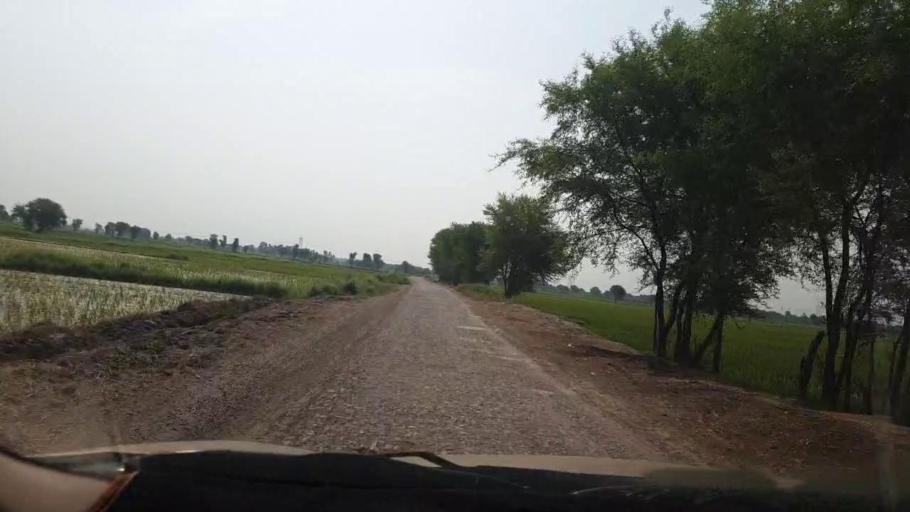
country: PK
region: Sindh
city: Goth Garelo
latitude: 27.4384
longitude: 68.0398
